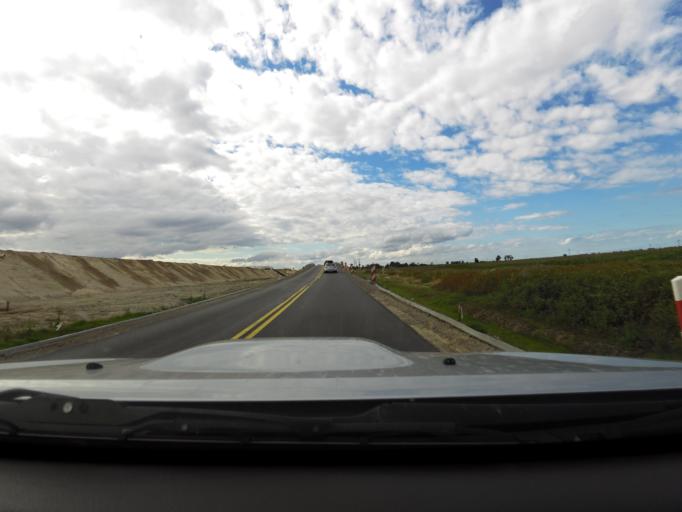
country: PL
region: Pomeranian Voivodeship
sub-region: Powiat nowodworski
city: Nowy Dwor Gdanski
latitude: 54.2342
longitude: 19.0410
